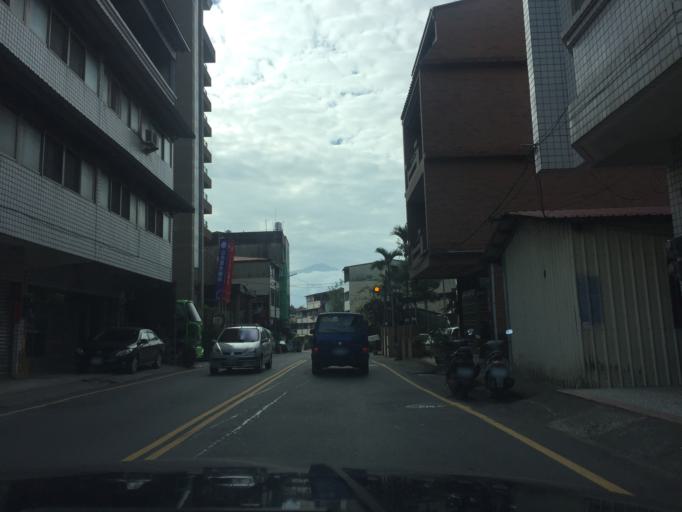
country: TW
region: Taiwan
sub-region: Nantou
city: Puli
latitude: 23.8665
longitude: 120.9027
